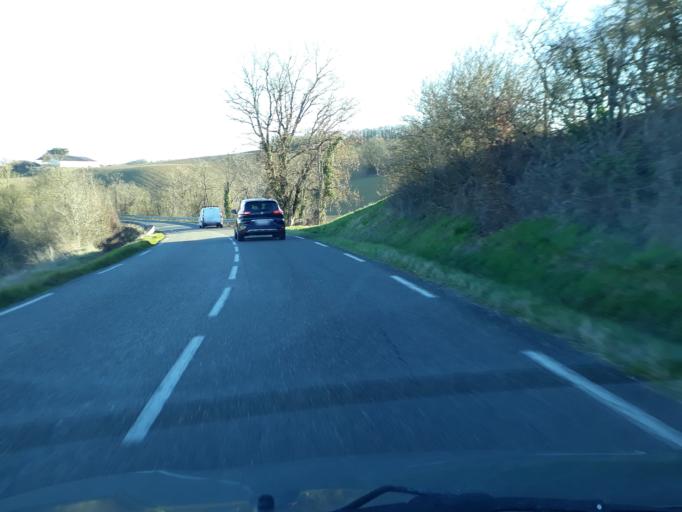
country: FR
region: Midi-Pyrenees
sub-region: Departement du Gers
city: Pavie
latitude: 43.6283
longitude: 0.6340
